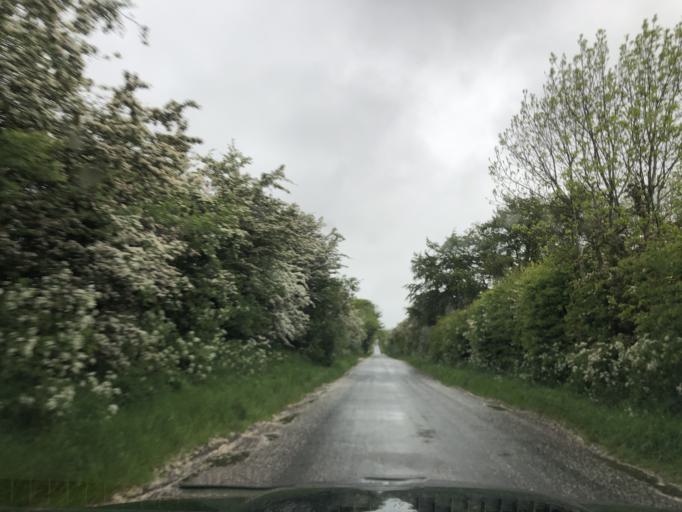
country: GB
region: Northern Ireland
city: Dunloy
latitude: 55.1274
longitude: -6.3689
